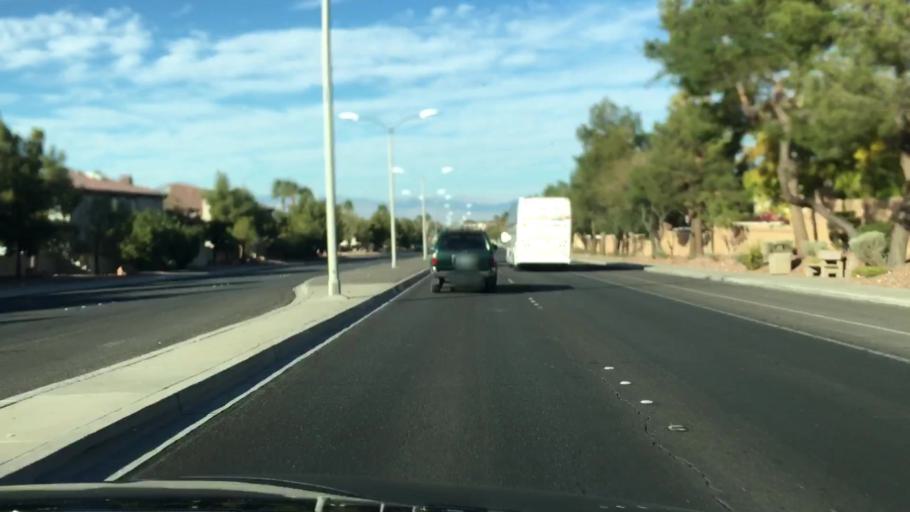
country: US
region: Nevada
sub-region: Clark County
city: Whitney
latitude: 36.0297
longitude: -115.1004
